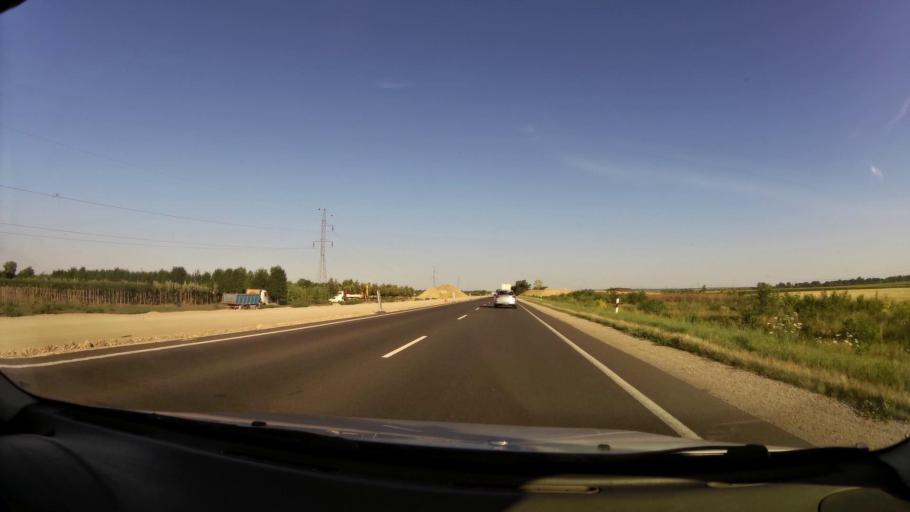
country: HU
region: Pest
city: Cegledbercel
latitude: 47.2132
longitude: 19.7373
